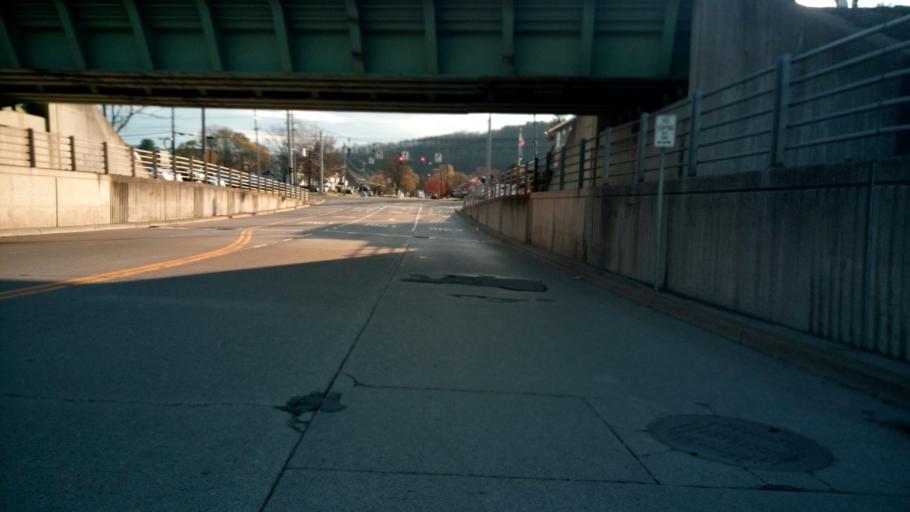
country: US
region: New York
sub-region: Chemung County
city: Elmira Heights
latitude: 42.1200
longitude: -76.8221
